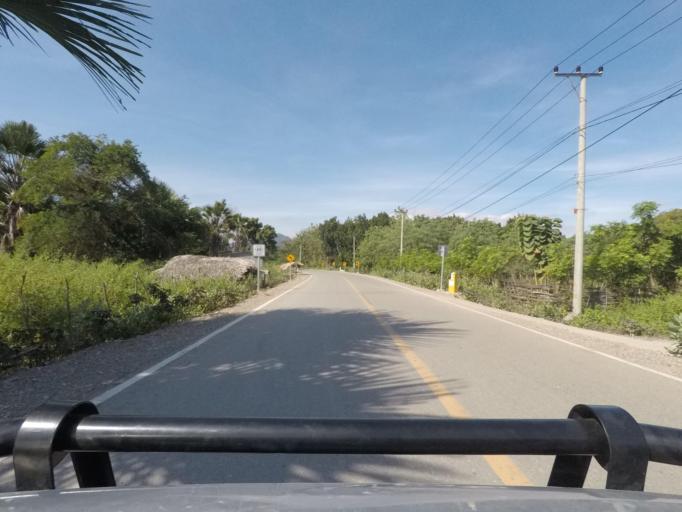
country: ID
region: East Nusa Tenggara
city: Atambua
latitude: -8.9570
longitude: 124.9558
